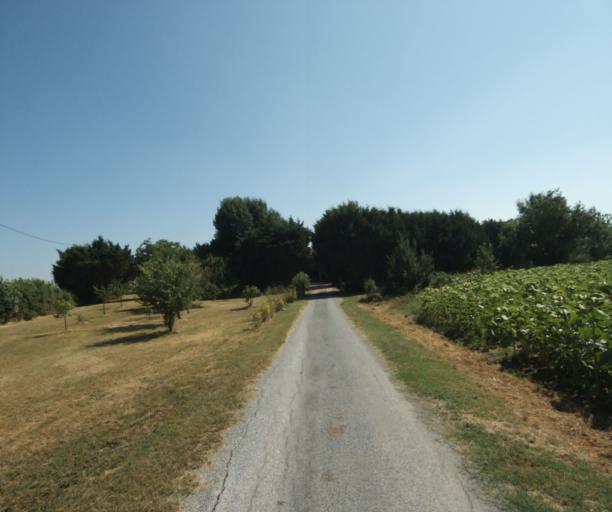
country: FR
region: Midi-Pyrenees
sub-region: Departement de la Haute-Garonne
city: Revel
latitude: 43.5032
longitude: 1.9564
